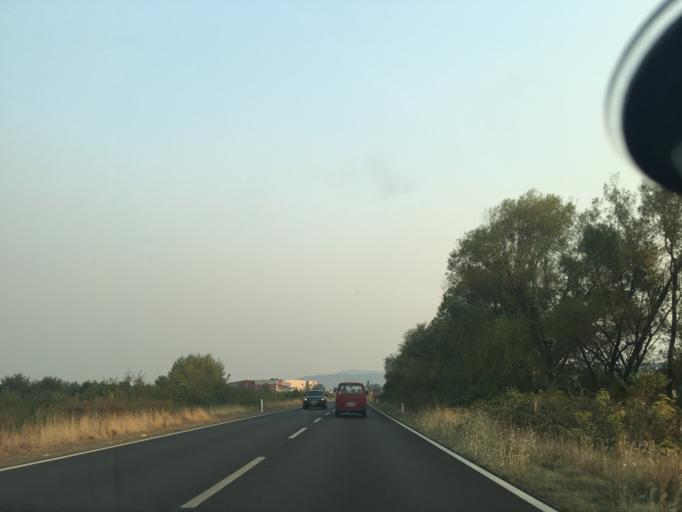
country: ME
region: Danilovgrad
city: Danilovgrad
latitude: 42.5357
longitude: 19.1136
